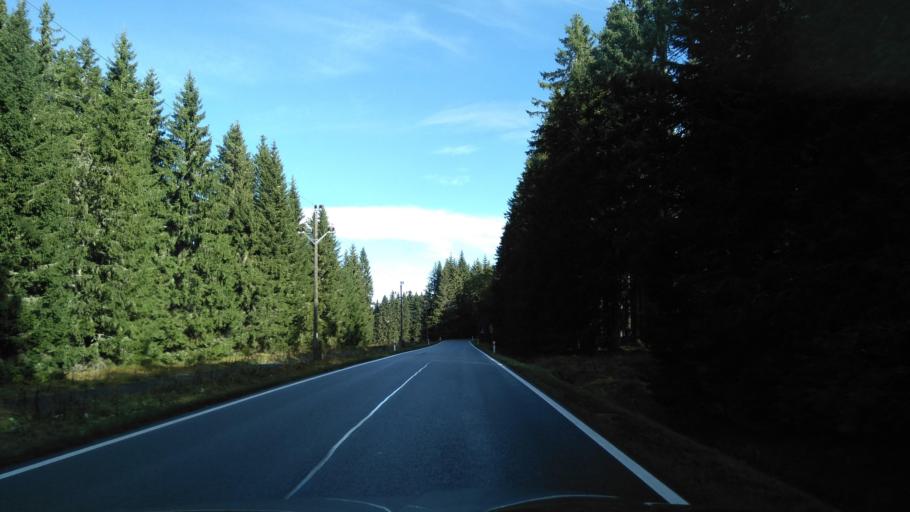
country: CZ
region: Jihocesky
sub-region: Okres Prachatice
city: Borova Lada
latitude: 49.0347
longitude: 13.5771
